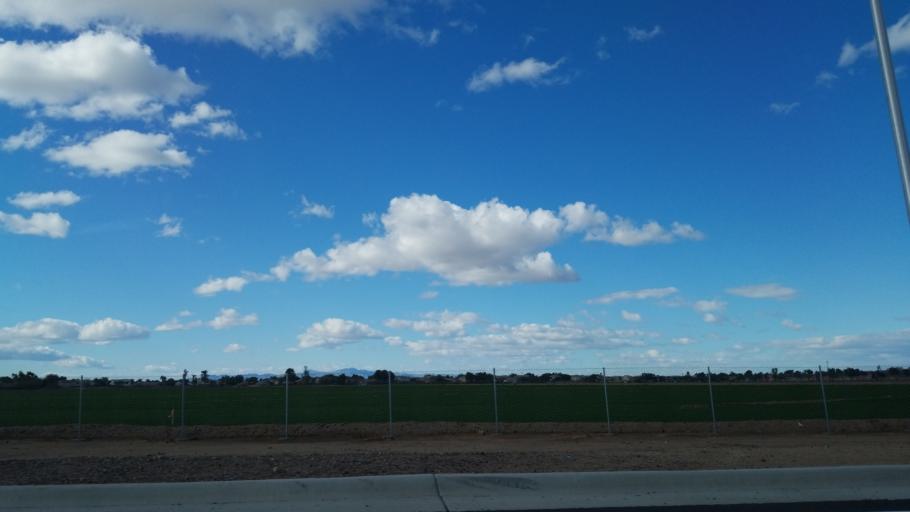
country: US
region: Arizona
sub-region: Maricopa County
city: Laveen
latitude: 33.4247
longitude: -112.1897
